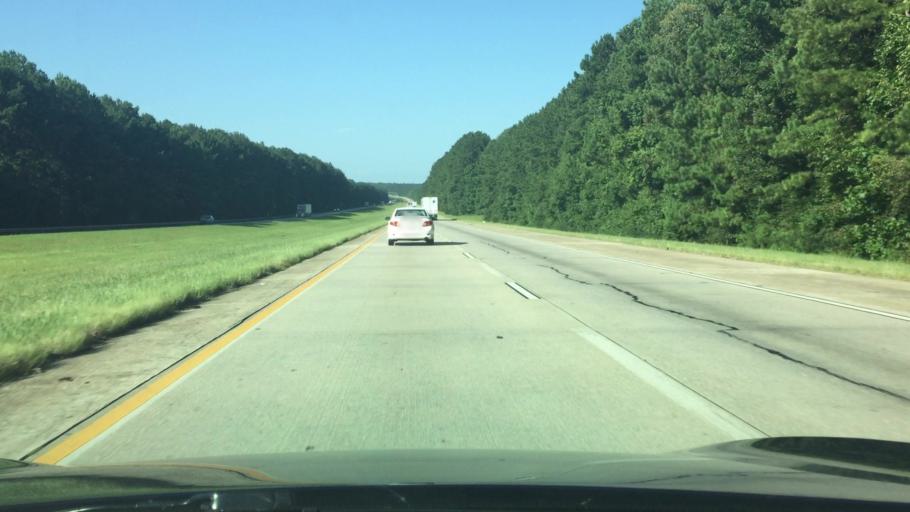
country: US
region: Georgia
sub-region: Troup County
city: Hogansville
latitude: 33.1469
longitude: -84.8788
